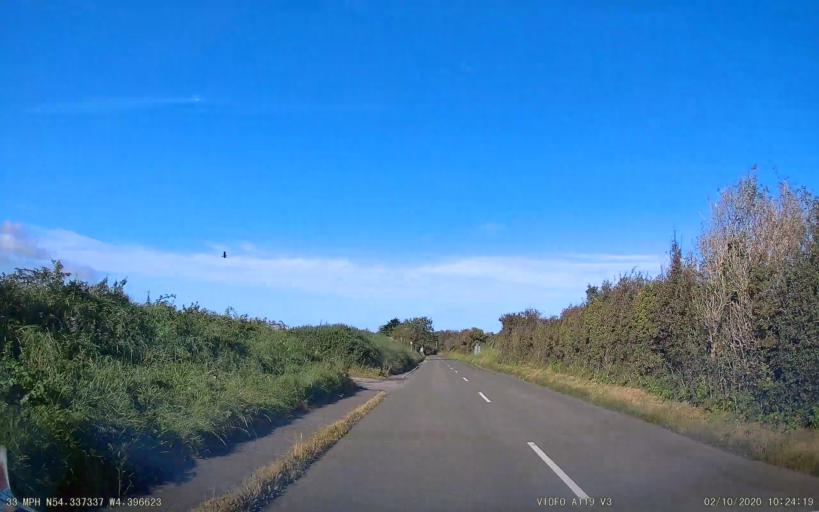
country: IM
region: Ramsey
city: Ramsey
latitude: 54.3373
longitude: -4.3966
